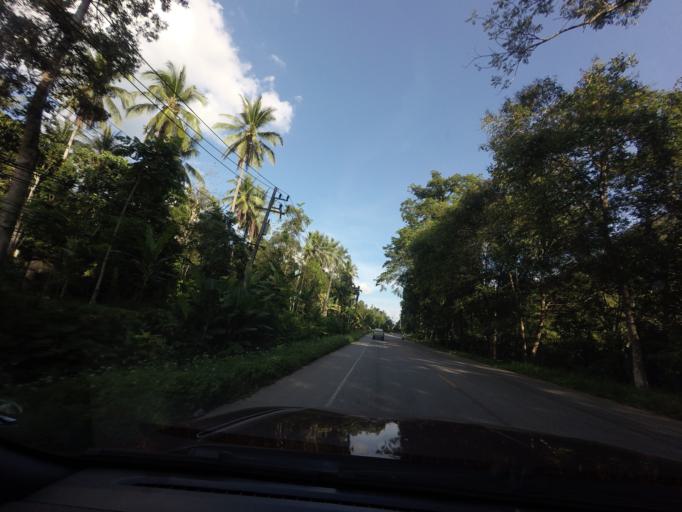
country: TH
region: Yala
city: Than To
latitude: 6.1783
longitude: 101.1750
